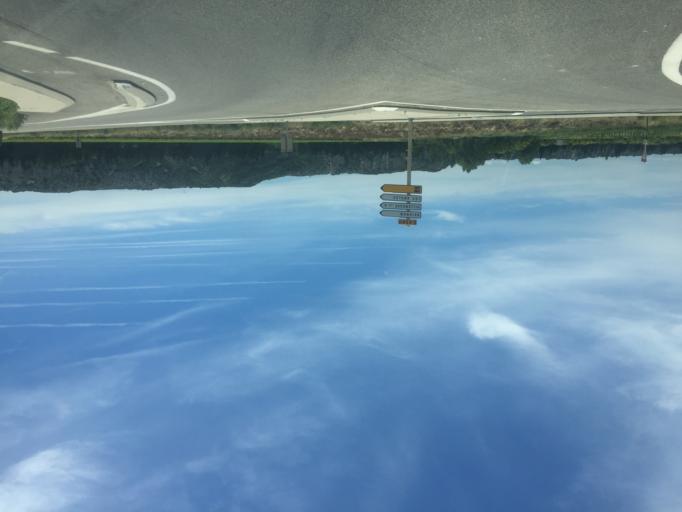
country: FR
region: Languedoc-Roussillon
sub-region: Departement du Gard
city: Pujaut
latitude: 43.9875
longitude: 4.7471
